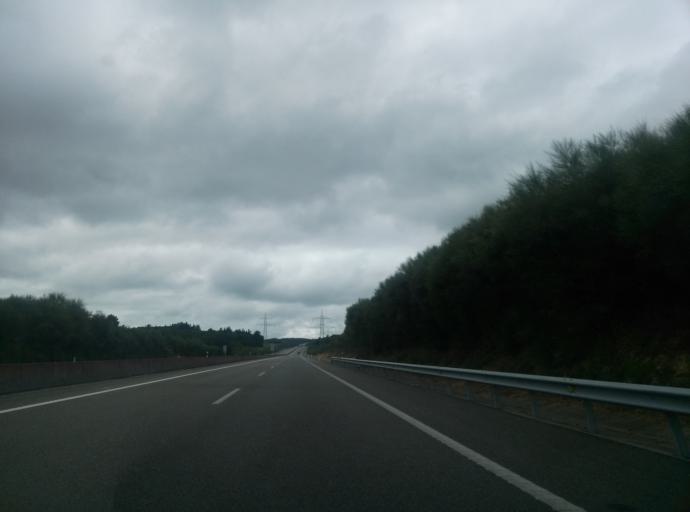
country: ES
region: Galicia
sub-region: Provincia de Lugo
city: Vilalba
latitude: 43.3278
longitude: -7.6963
